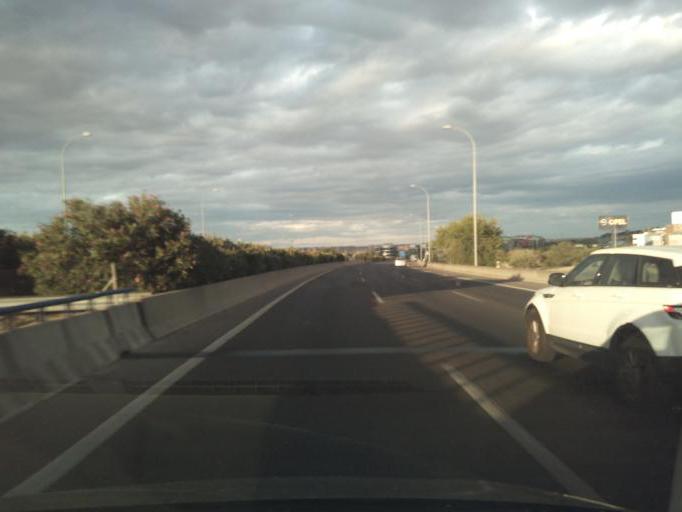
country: ES
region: Madrid
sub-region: Provincia de Madrid
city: Alcobendas
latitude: 40.5323
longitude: -3.6404
